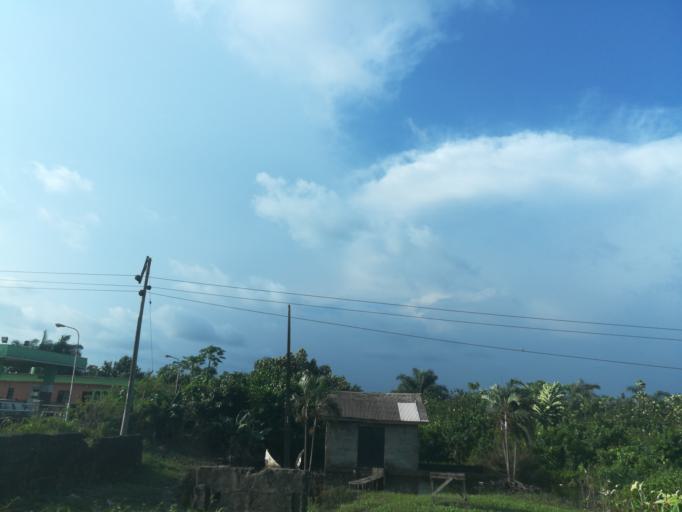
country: NG
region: Ogun
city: Ado Odo
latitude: 6.4863
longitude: 3.0622
